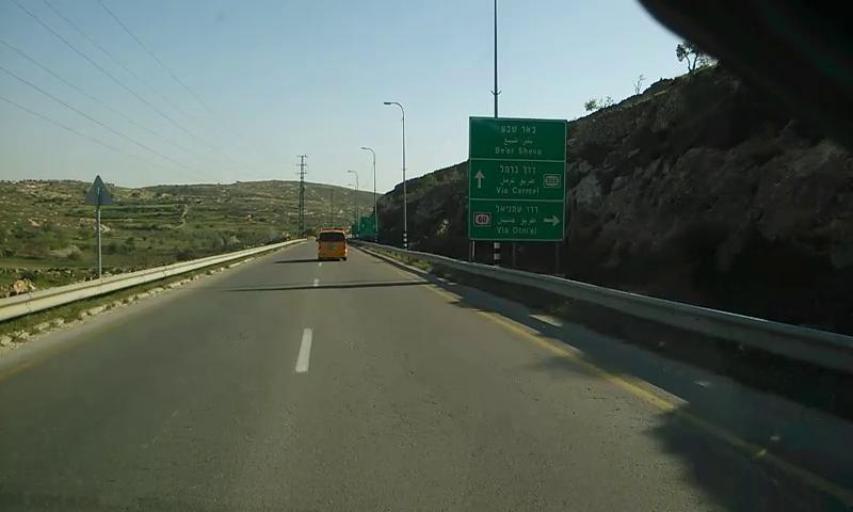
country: PS
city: Khallat ad Dar
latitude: 31.5056
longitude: 35.1333
